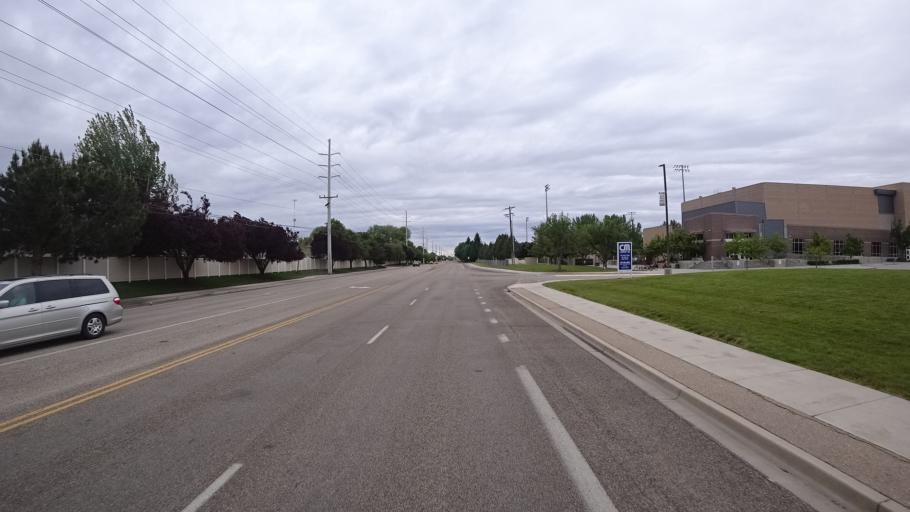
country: US
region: Idaho
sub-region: Ada County
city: Eagle
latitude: 43.6486
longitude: -116.3367
